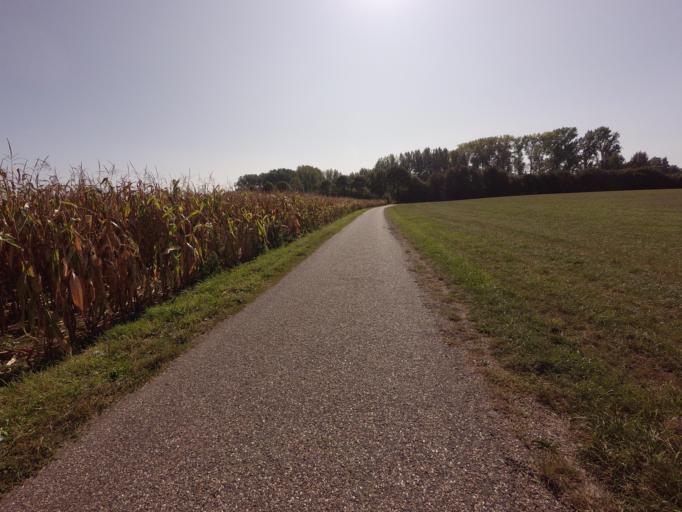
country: NL
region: Limburg
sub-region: Gemeente Roerdalen
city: Melick
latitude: 51.1495
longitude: 6.0339
